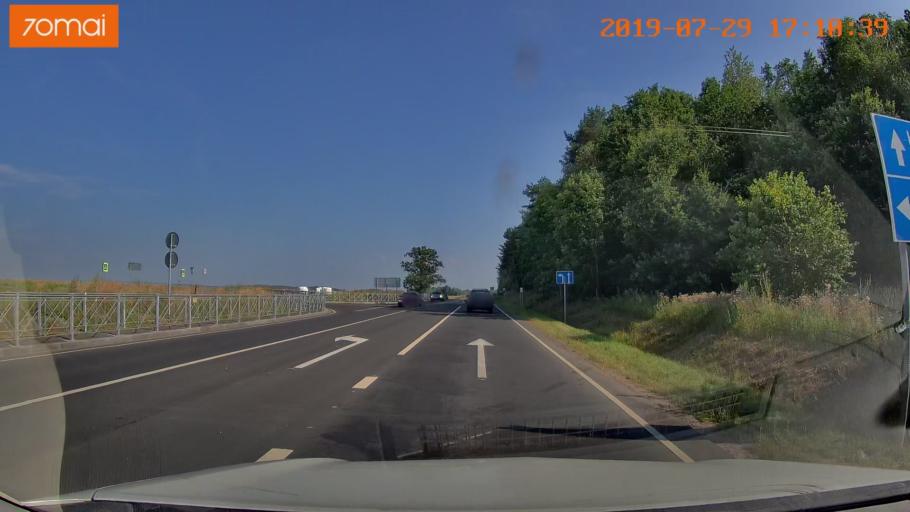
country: RU
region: Kaliningrad
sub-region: Gorod Kaliningrad
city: Kaliningrad
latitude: 54.8007
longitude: 20.3710
